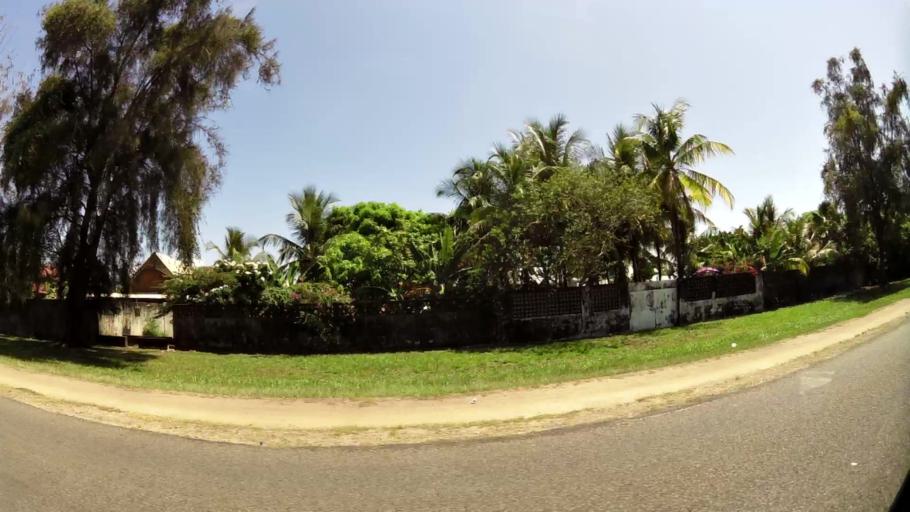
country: GF
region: Guyane
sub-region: Guyane
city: Kourou
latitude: 5.1714
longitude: -52.6491
